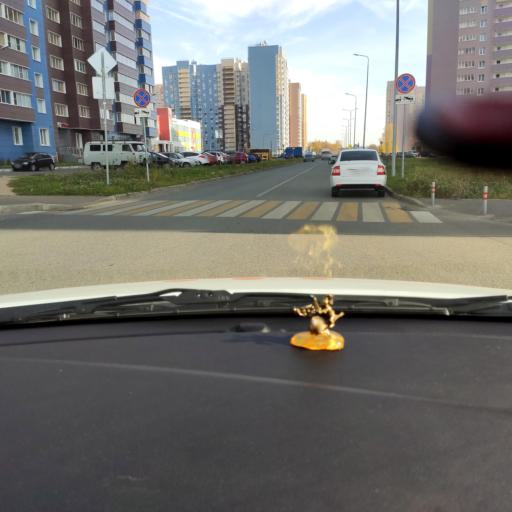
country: RU
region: Tatarstan
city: Osinovo
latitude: 55.8635
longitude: 48.8779
